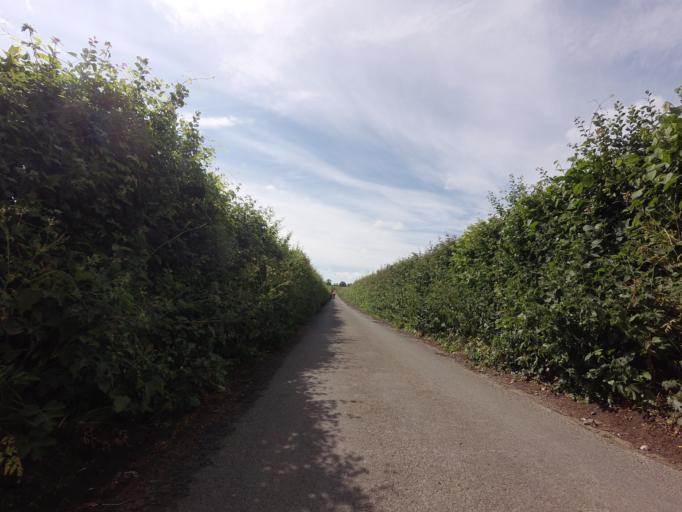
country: GB
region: England
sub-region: Greater London
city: Orpington
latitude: 51.3659
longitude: 0.1303
